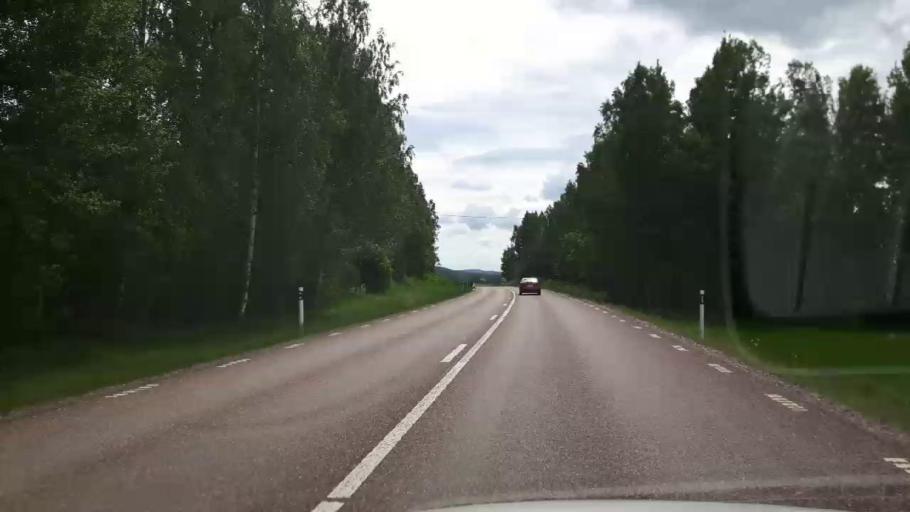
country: SE
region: Dalarna
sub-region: Hedemora Kommun
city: Hedemora
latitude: 60.3359
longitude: 15.9447
